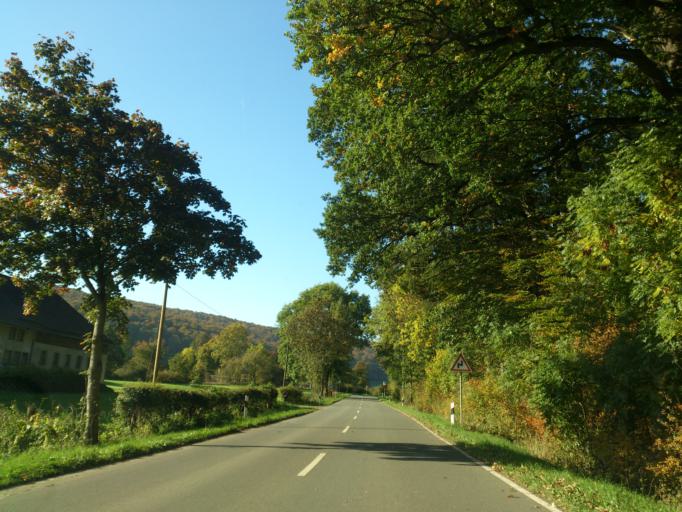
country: DE
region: North Rhine-Westphalia
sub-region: Regierungsbezirk Detmold
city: Willebadessen
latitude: 51.5740
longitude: 9.0402
